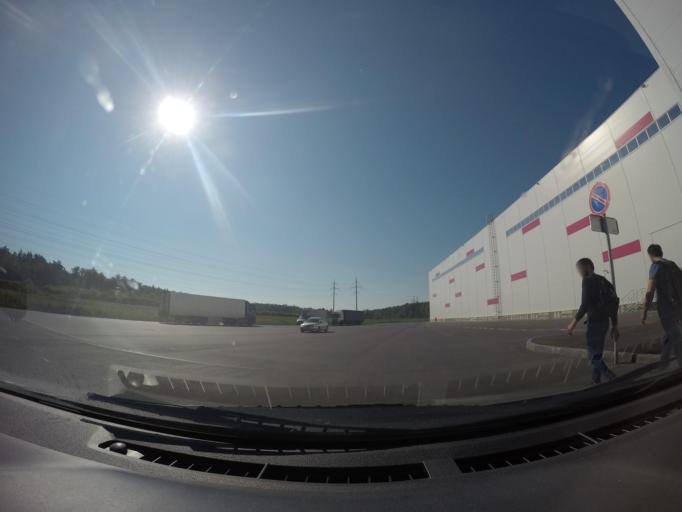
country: RU
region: Moskovskaya
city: Fryazevo
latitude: 55.7433
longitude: 38.4225
